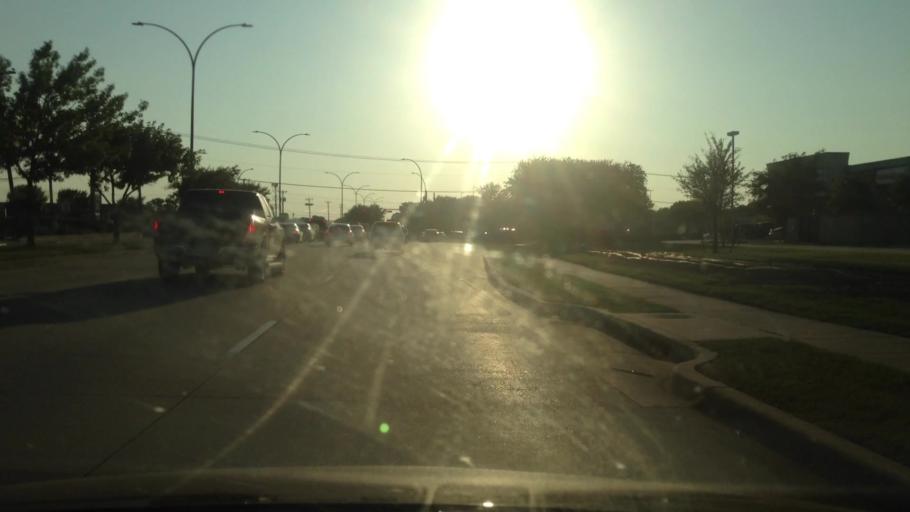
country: US
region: Texas
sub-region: Tarrant County
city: Dalworthington Gardens
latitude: 32.6449
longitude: -97.1138
